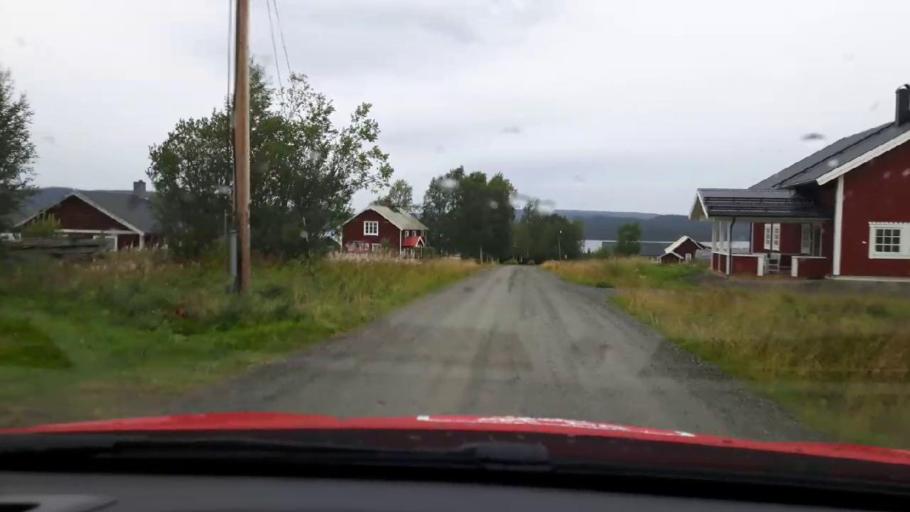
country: SE
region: Jaemtland
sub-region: Are Kommun
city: Are
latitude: 63.5146
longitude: 12.7130
